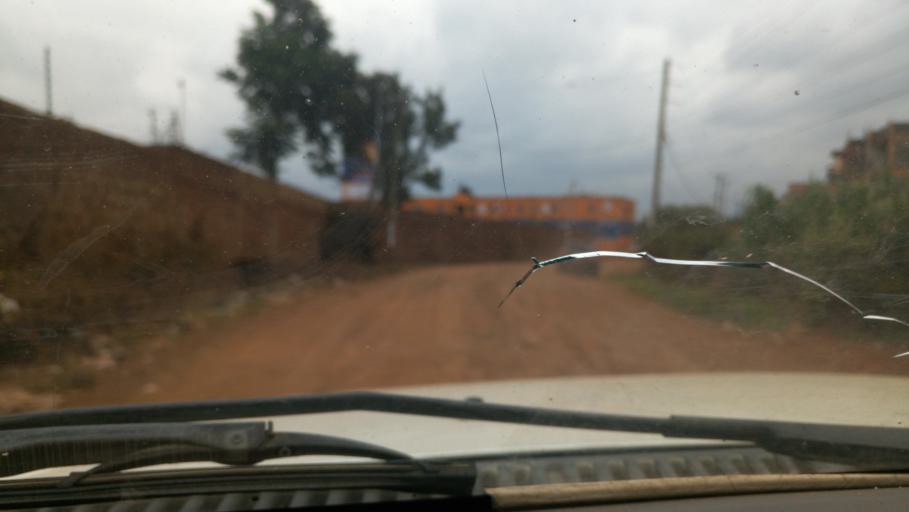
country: KE
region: Nairobi Area
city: Pumwani
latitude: -1.2290
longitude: 36.8786
